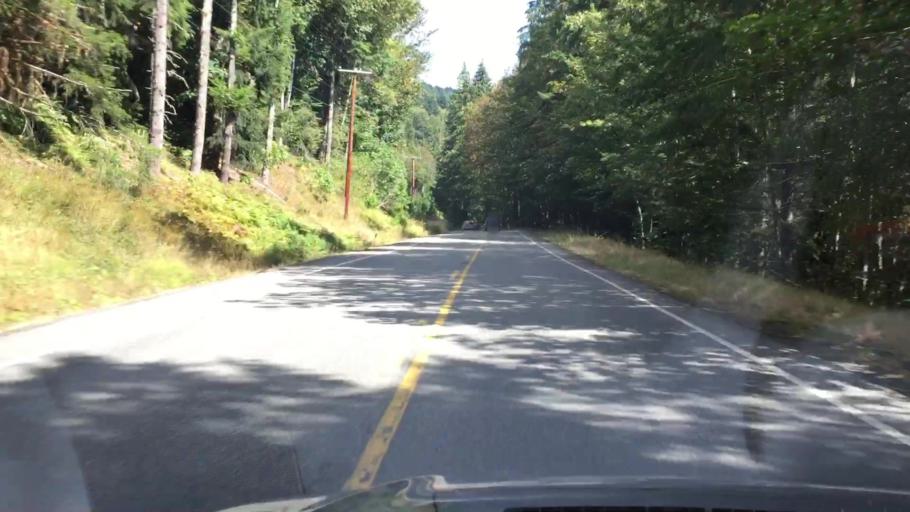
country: US
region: Washington
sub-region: Pierce County
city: Eatonville
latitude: 46.7555
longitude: -121.9543
